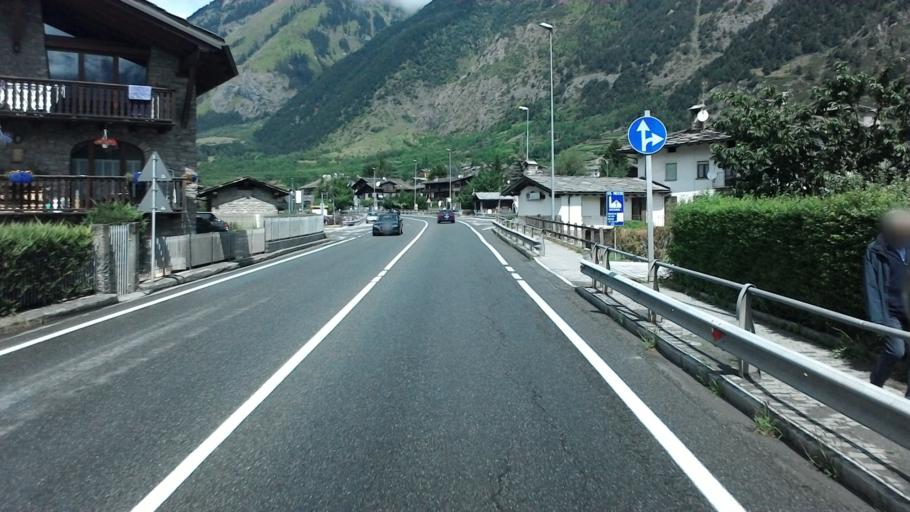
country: IT
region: Aosta Valley
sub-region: Valle d'Aosta
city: Morgex
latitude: 45.7573
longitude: 7.0372
